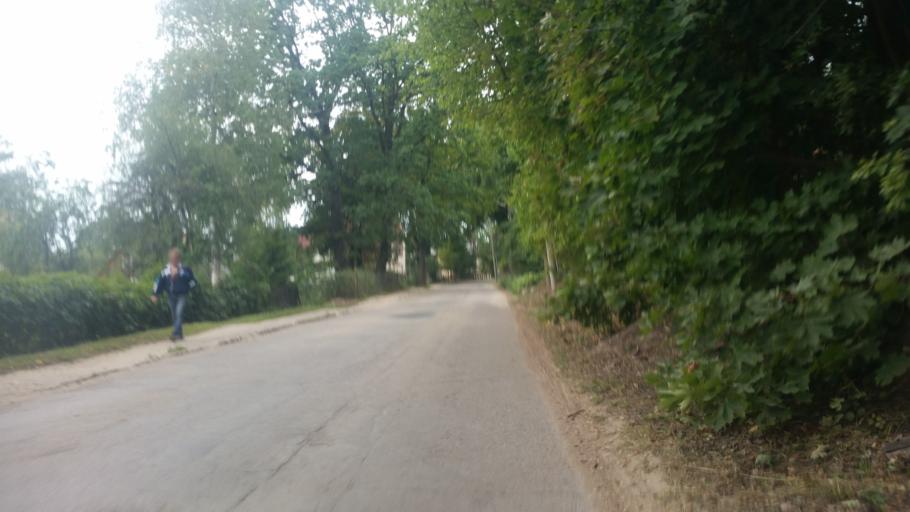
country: LV
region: Ogre
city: Ogre
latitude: 56.8099
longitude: 24.6187
